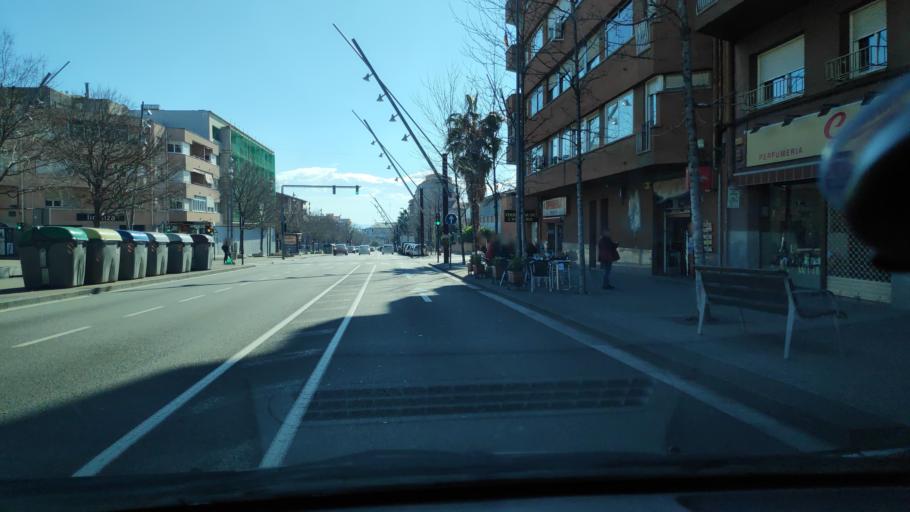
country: ES
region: Catalonia
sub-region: Provincia de Barcelona
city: Terrassa
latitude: 41.5629
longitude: 2.0274
